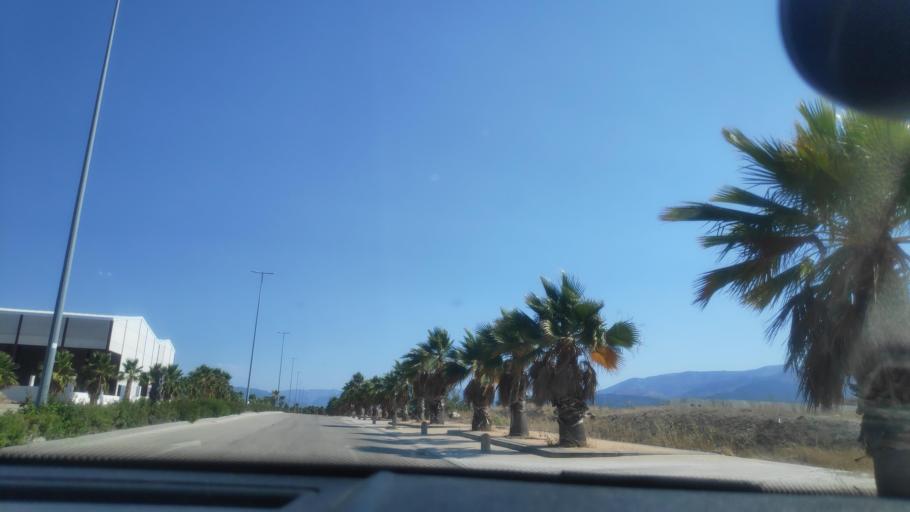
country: ES
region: Andalusia
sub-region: Provincia de Jaen
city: Jaen
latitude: 37.8258
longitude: -3.7763
